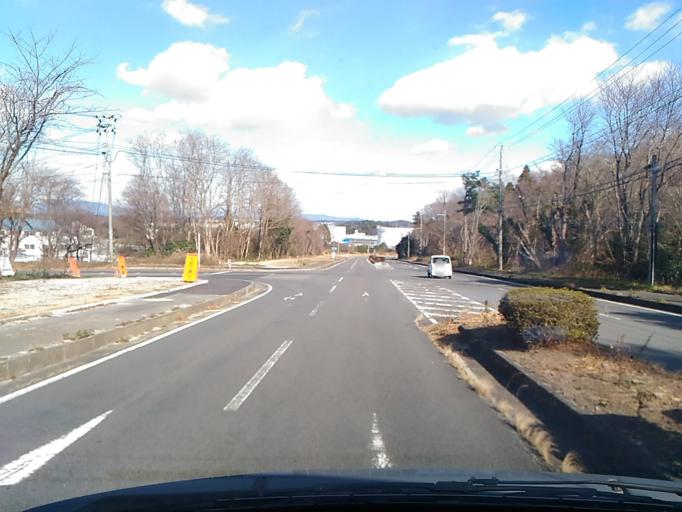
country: JP
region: Fukushima
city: Iwaki
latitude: 36.9247
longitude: 140.8528
